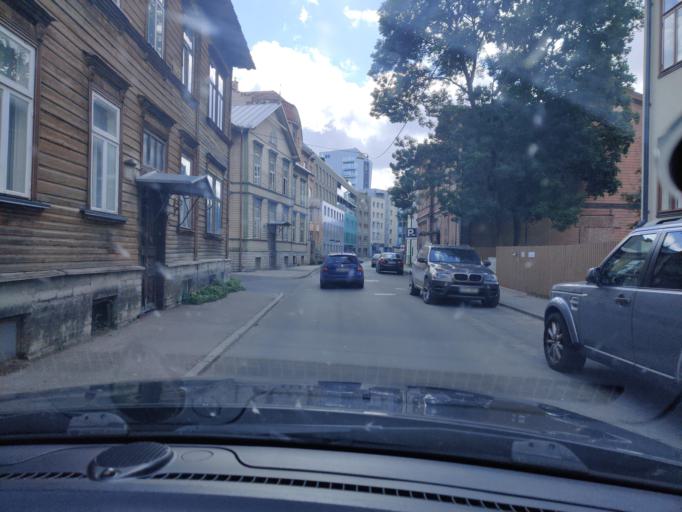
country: EE
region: Harju
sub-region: Tallinna linn
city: Tallinn
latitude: 59.4301
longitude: 24.7483
